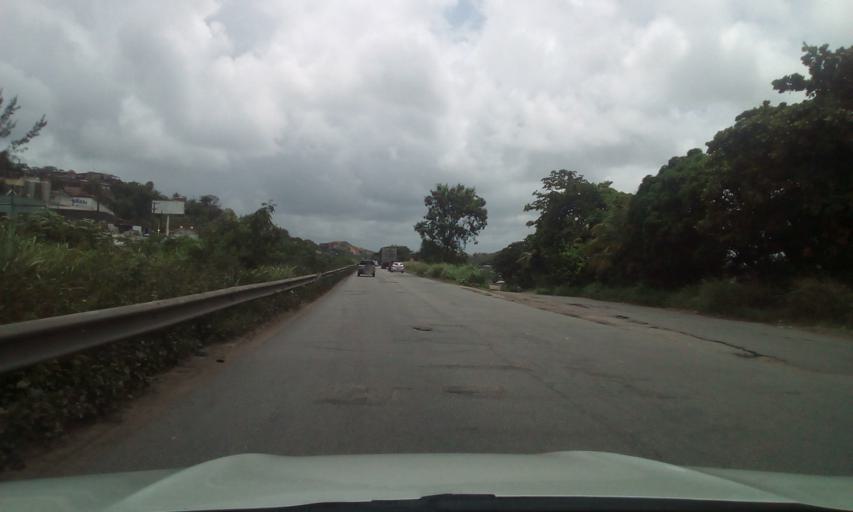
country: BR
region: Pernambuco
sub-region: Jaboatao Dos Guararapes
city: Jaboatao dos Guararapes
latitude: -8.1187
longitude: -34.9432
